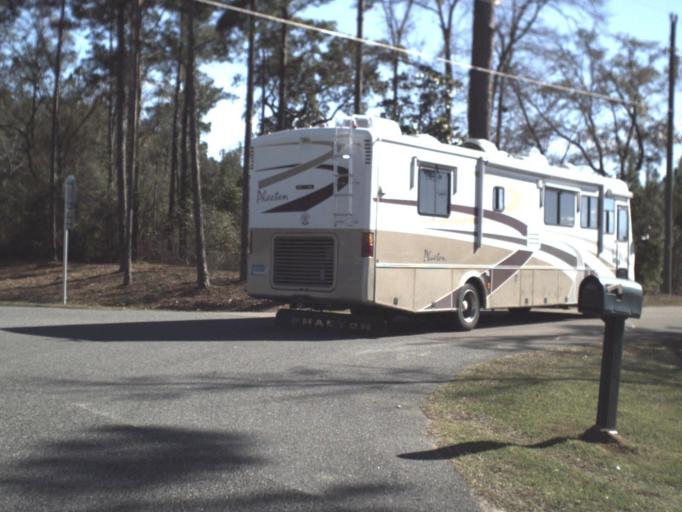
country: US
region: Florida
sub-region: Gadsden County
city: Midway
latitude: 30.5012
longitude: -84.4501
